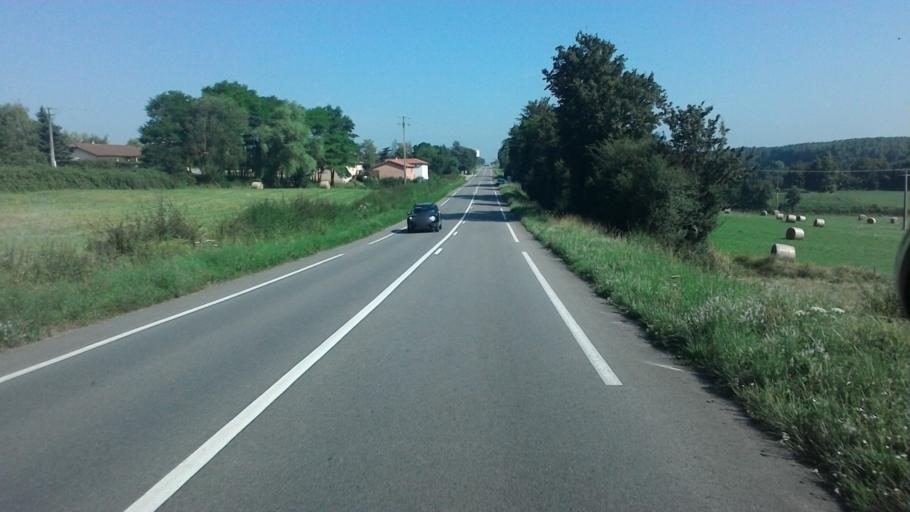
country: FR
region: Rhone-Alpes
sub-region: Departement de l'Ain
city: Montrevel-en-Bresse
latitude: 46.3521
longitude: 5.1248
